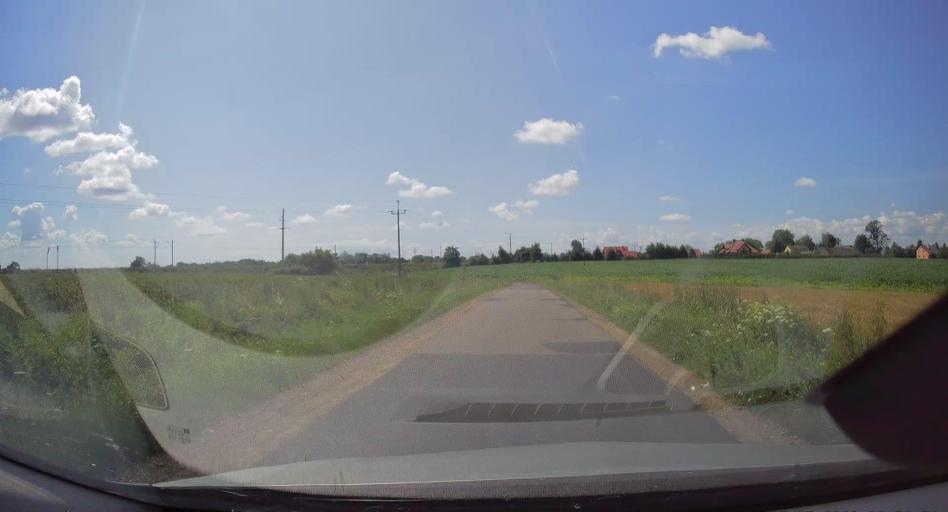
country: PL
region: Subcarpathian Voivodeship
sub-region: Powiat jaroslawski
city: Sosnica
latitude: 49.8704
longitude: 22.8593
